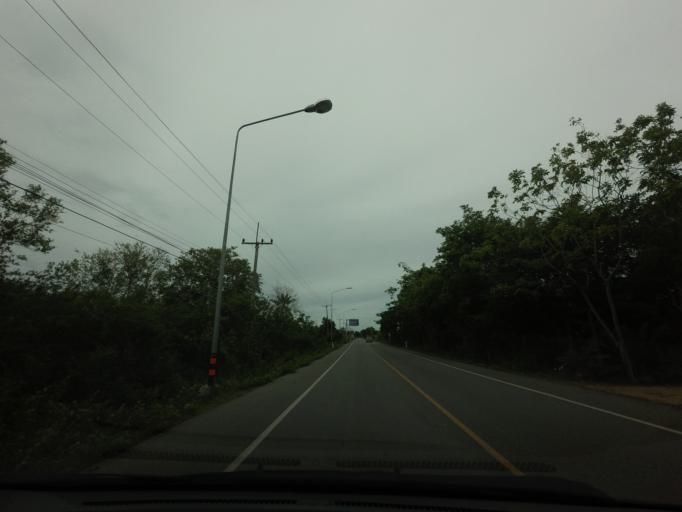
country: TH
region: Phetchaburi
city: Cha-am
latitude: 12.8432
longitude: 99.9930
